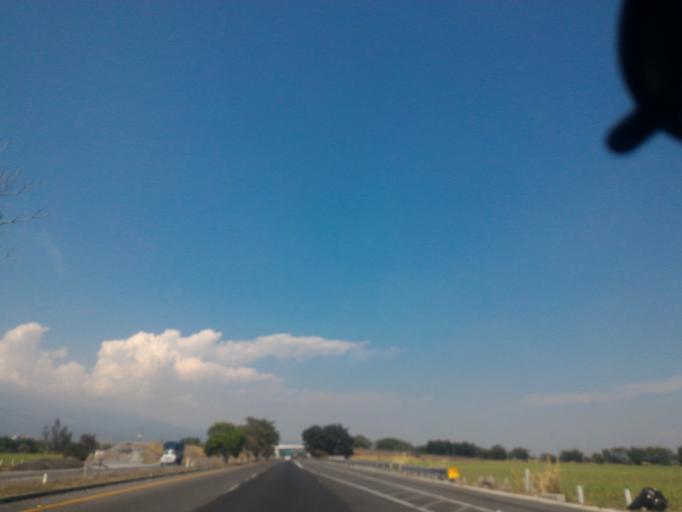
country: MX
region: Colima
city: Queseria
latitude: 19.3527
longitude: -103.5659
